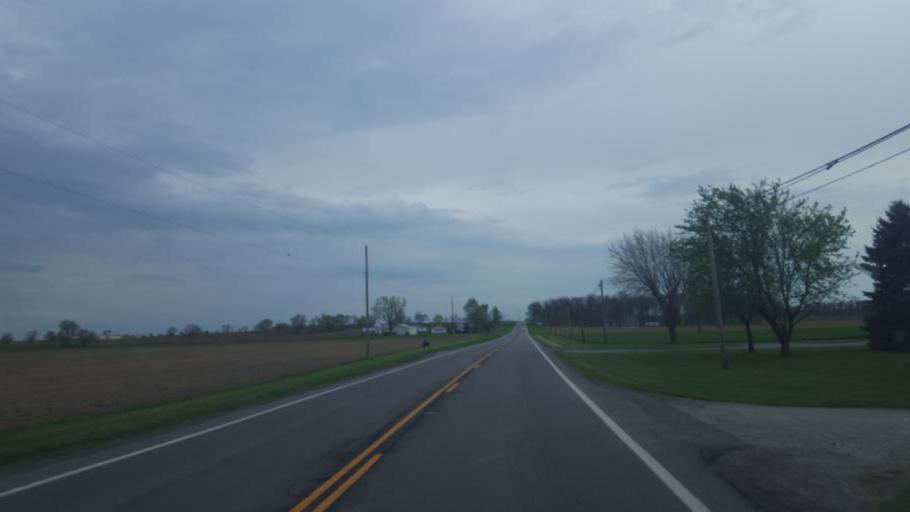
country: US
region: Ohio
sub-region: Wyandot County
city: Carey
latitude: 40.9911
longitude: -83.3826
